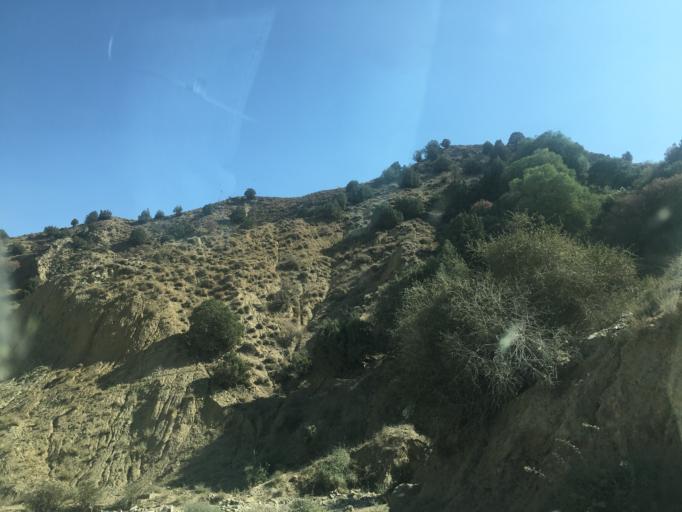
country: TM
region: Ahal
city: Baharly
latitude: 38.4416
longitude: 57.0471
